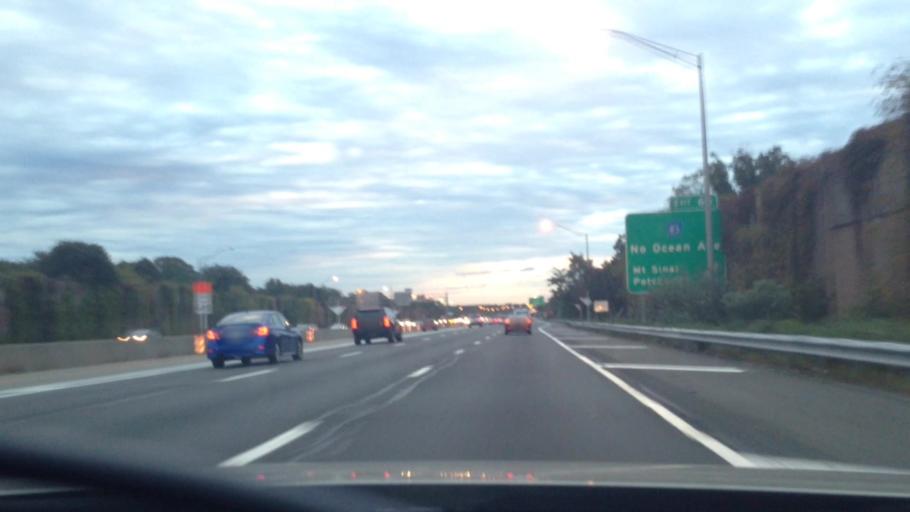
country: US
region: New York
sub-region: Suffolk County
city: Farmingville
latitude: 40.8221
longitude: -73.0348
